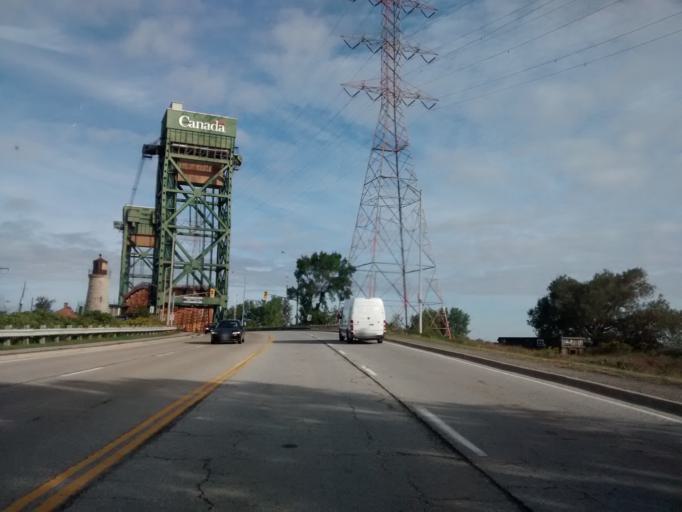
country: CA
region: Ontario
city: Hamilton
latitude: 43.2971
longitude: -79.7944
